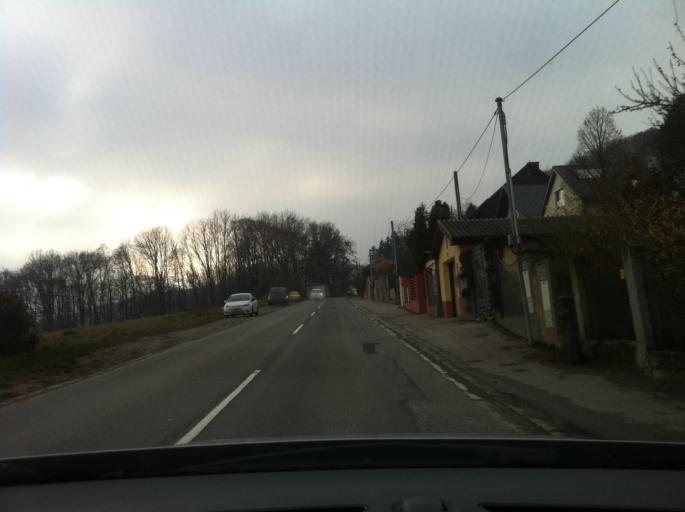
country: AT
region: Lower Austria
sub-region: Politischer Bezirk Wien-Umgebung
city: Klosterneuburg
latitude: 48.2452
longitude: 16.2616
